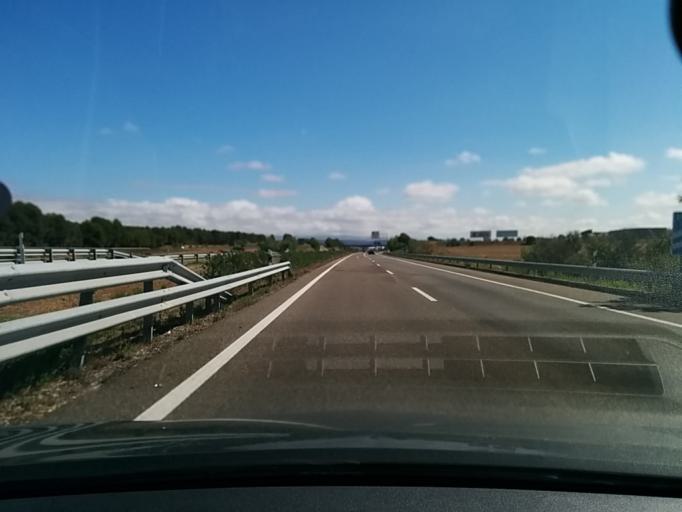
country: ES
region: Aragon
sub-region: Provincia de Huesca
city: Huesca
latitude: 42.1118
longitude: -0.4489
